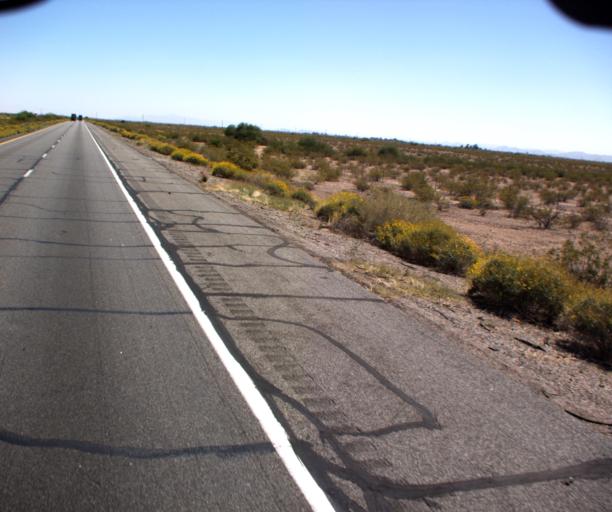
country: US
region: Arizona
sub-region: Maricopa County
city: Buckeye
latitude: 33.4768
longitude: -112.8457
